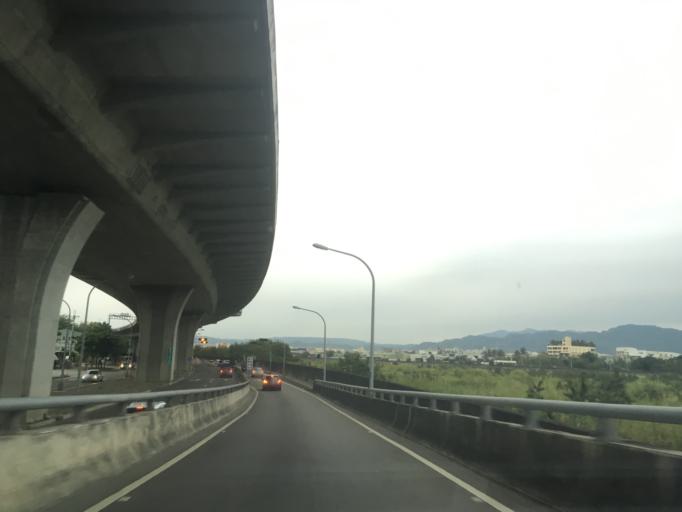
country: TW
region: Taiwan
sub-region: Taichung City
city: Taichung
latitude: 24.1127
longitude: 120.6980
